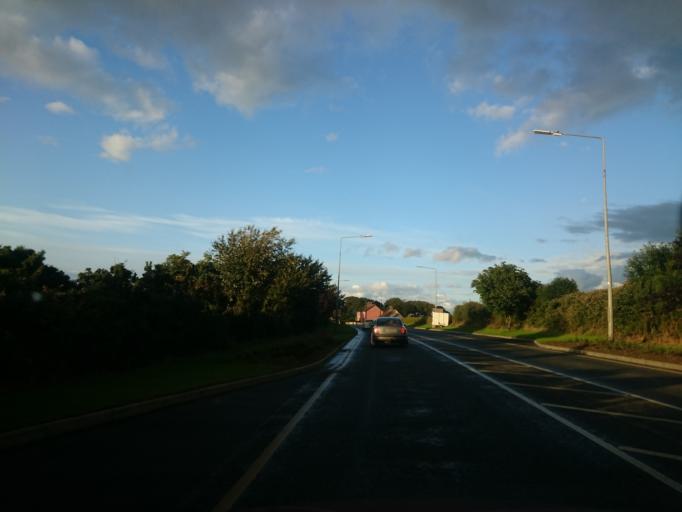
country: IE
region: Leinster
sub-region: Loch Garman
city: Ferns
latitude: 52.6117
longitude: -6.4355
